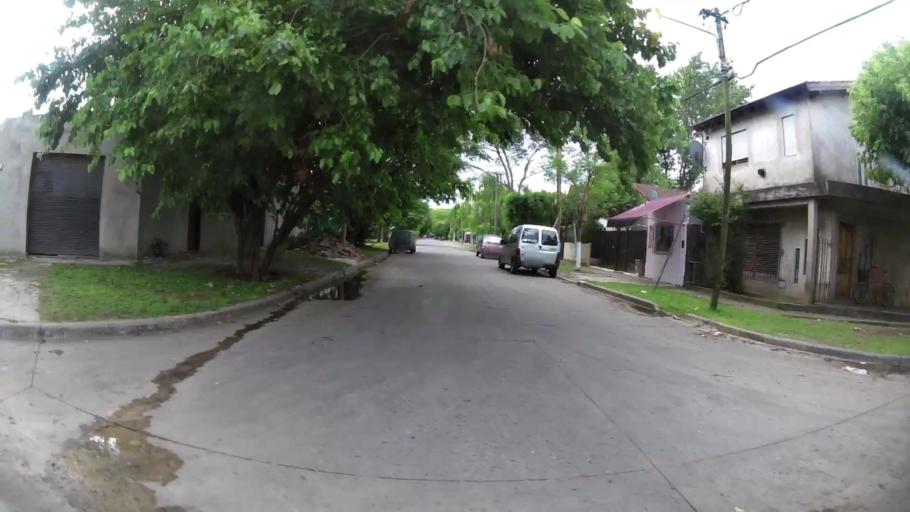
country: AR
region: Buenos Aires
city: Ituzaingo
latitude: -34.6339
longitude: -58.6789
